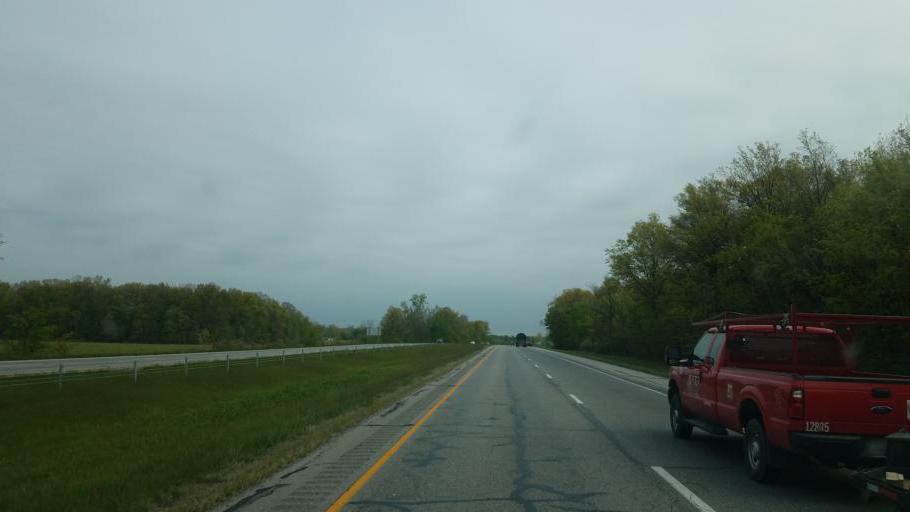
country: US
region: Indiana
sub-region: Allen County
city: Huntertown
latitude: 41.2135
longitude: -85.1047
